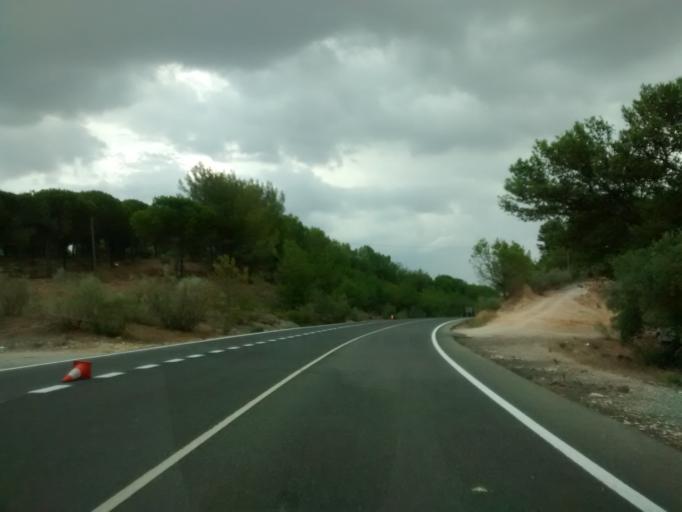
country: ES
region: Andalusia
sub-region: Provincia de Cadiz
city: Bornos
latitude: 36.8155
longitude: -5.7591
